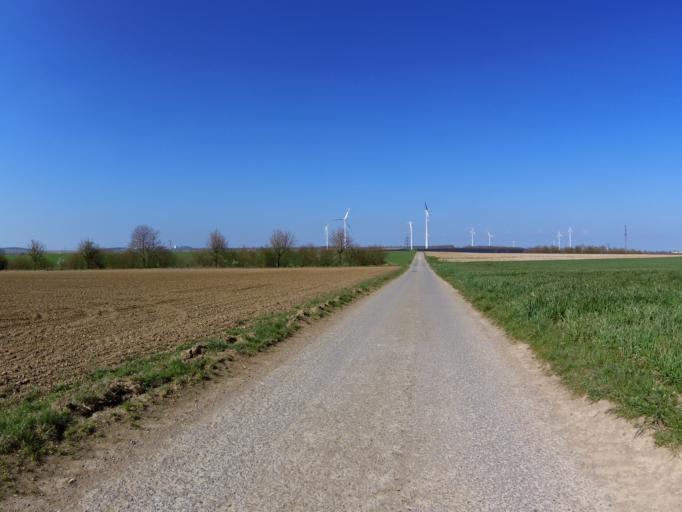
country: DE
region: Bavaria
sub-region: Regierungsbezirk Unterfranken
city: Biebelried
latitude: 49.7396
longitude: 10.1012
